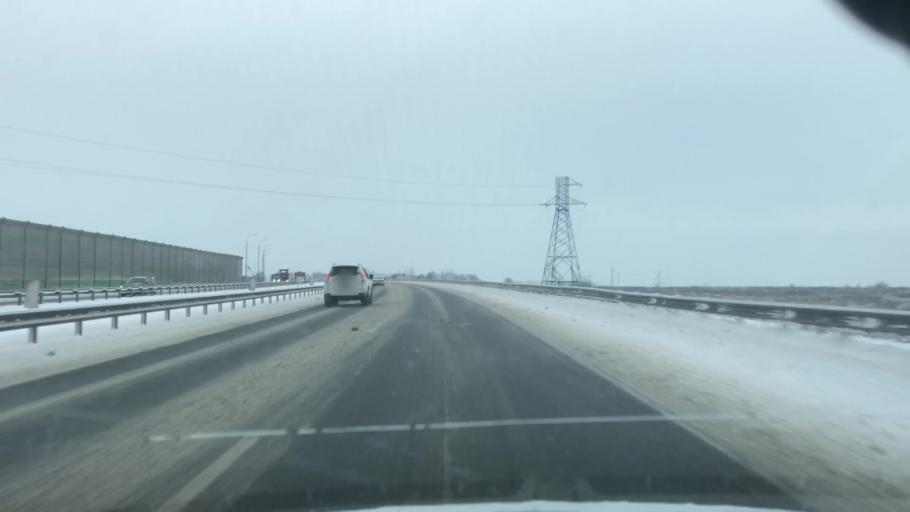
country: RU
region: Moskovskaya
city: Mikhnevo
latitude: 55.1187
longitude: 37.9284
